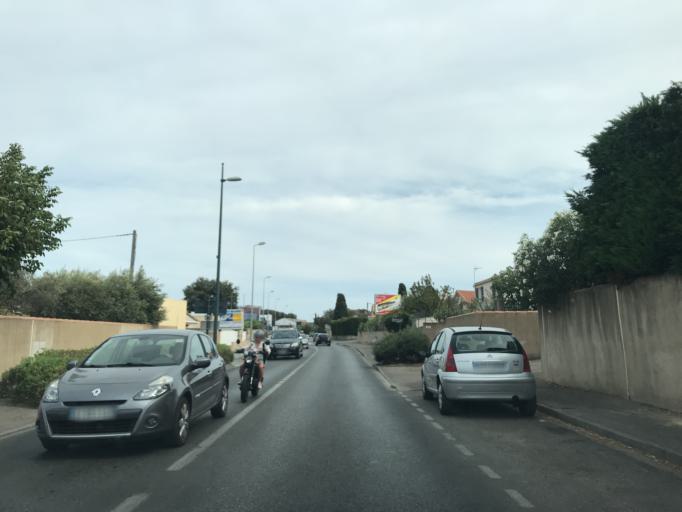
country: FR
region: Provence-Alpes-Cote d'Azur
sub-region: Departement du Var
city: Six-Fours-les-Plages
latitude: 43.0884
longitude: 5.8528
